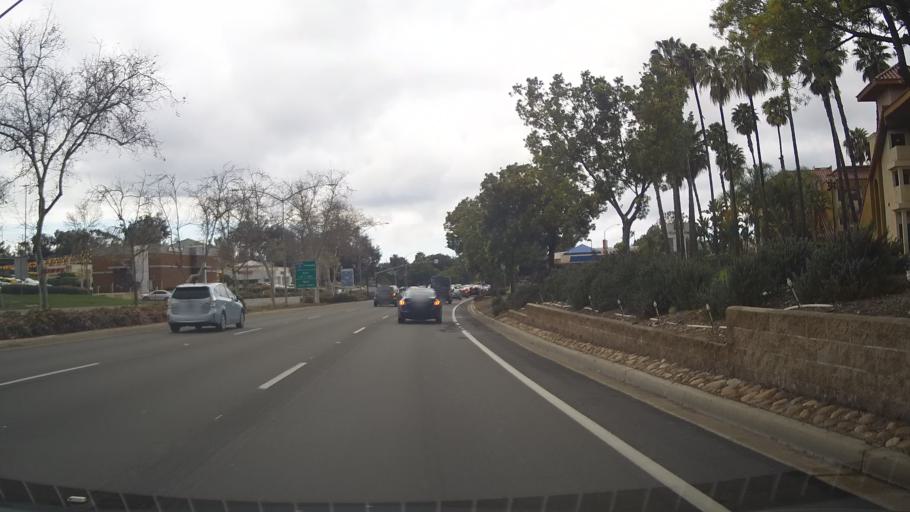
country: US
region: California
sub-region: San Diego County
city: La Mesa
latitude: 32.7746
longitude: -117.0251
